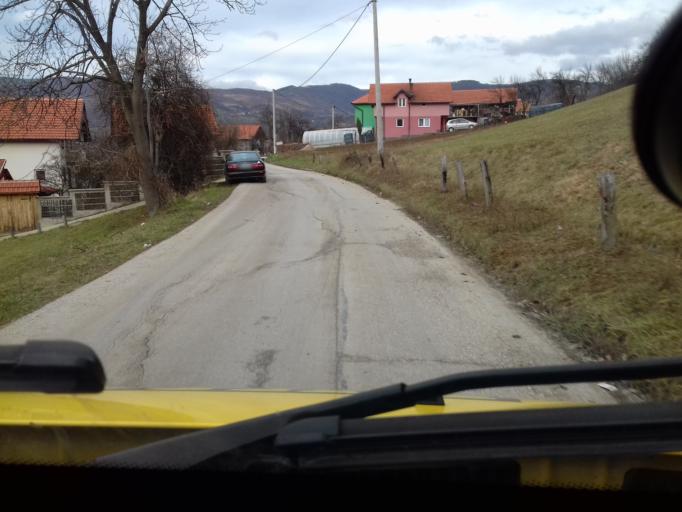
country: BA
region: Federation of Bosnia and Herzegovina
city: Zenica
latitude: 44.1612
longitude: 17.9698
